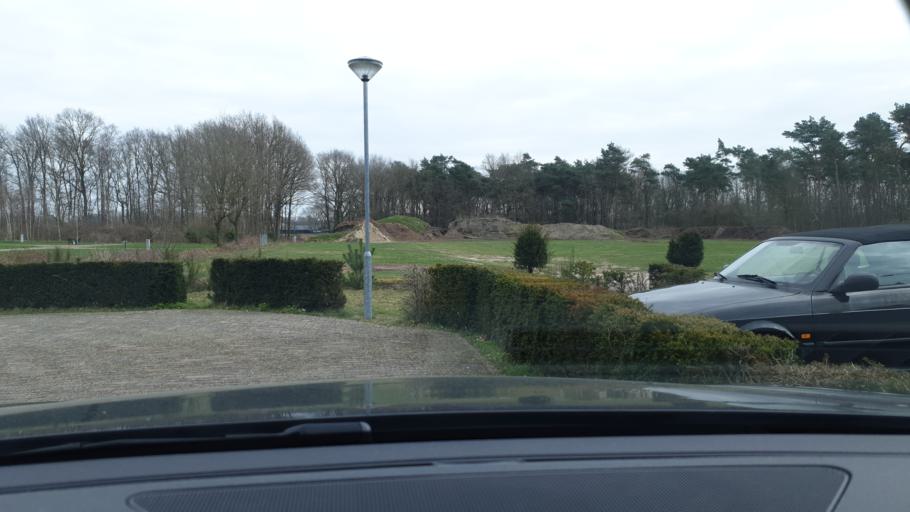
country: NL
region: North Brabant
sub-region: Gemeente Oirschot
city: Oostelbeers
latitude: 51.4126
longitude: 5.2748
